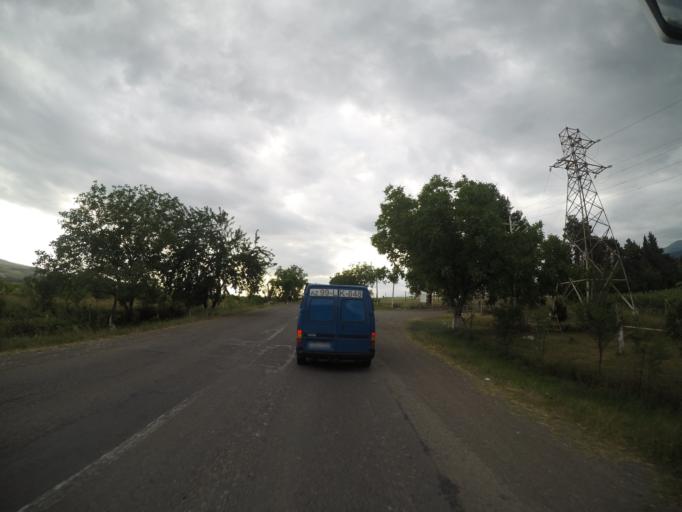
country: AZ
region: Ismayilli
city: Ismayilli
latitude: 40.7767
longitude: 48.1944
